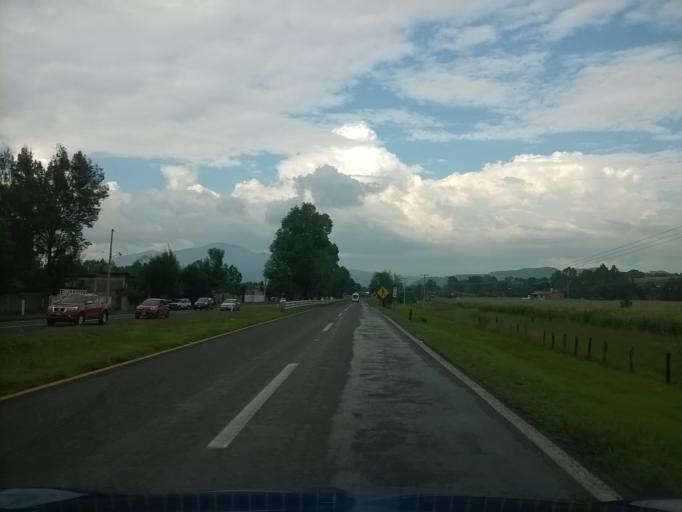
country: MX
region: Michoacan
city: Huiramba
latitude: 19.5388
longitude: -101.4637
